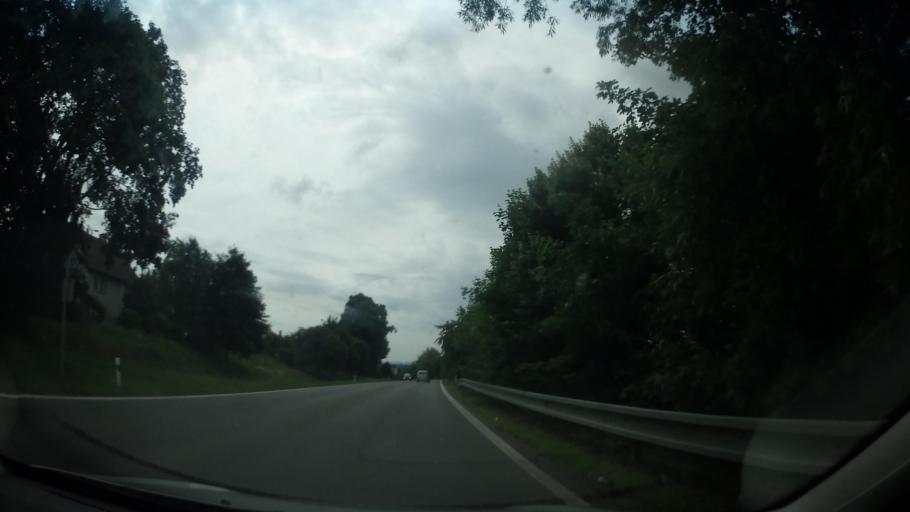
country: CZ
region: Vysocina
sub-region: Okres Zd'ar nad Sazavou
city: Nove Mesto na Morave
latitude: 49.5750
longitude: 16.0772
